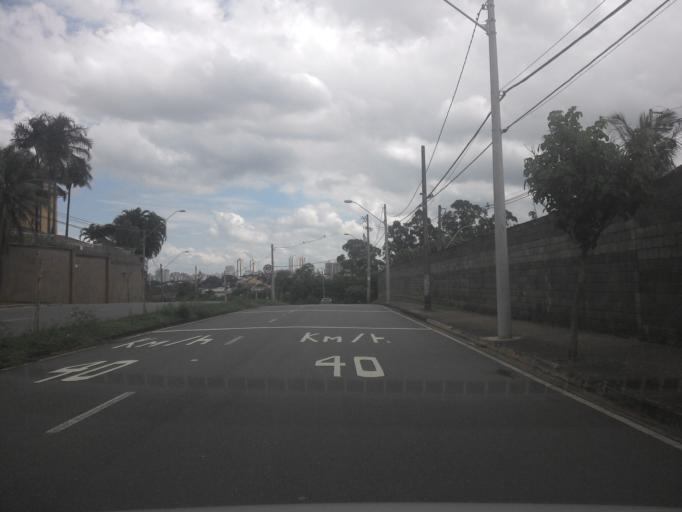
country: BR
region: Sao Paulo
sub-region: Campinas
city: Campinas
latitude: -22.8677
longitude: -47.0313
